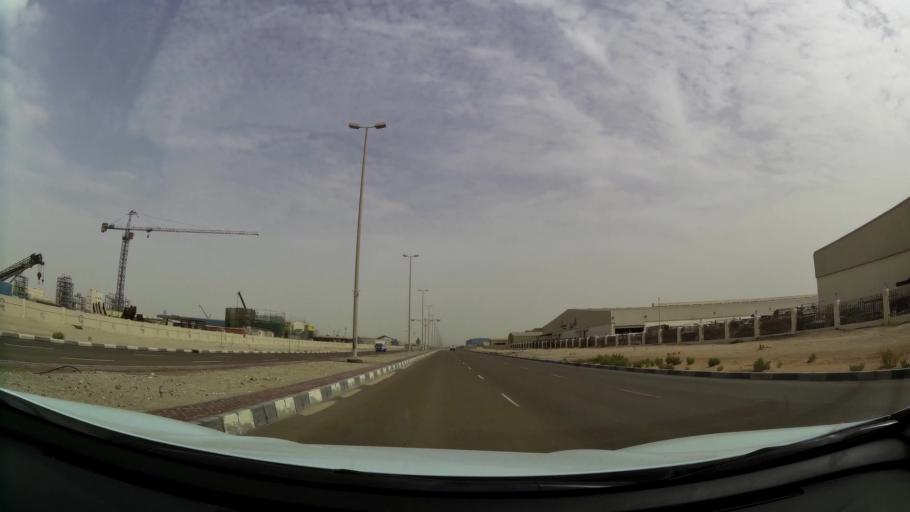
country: AE
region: Abu Dhabi
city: Abu Dhabi
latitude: 24.3226
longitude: 54.4862
